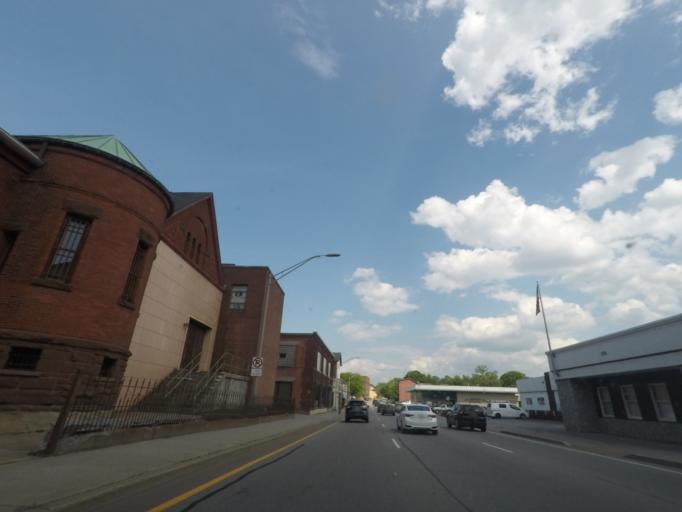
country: US
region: New York
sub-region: Dutchess County
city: Poughkeepsie
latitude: 41.7018
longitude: -73.9294
